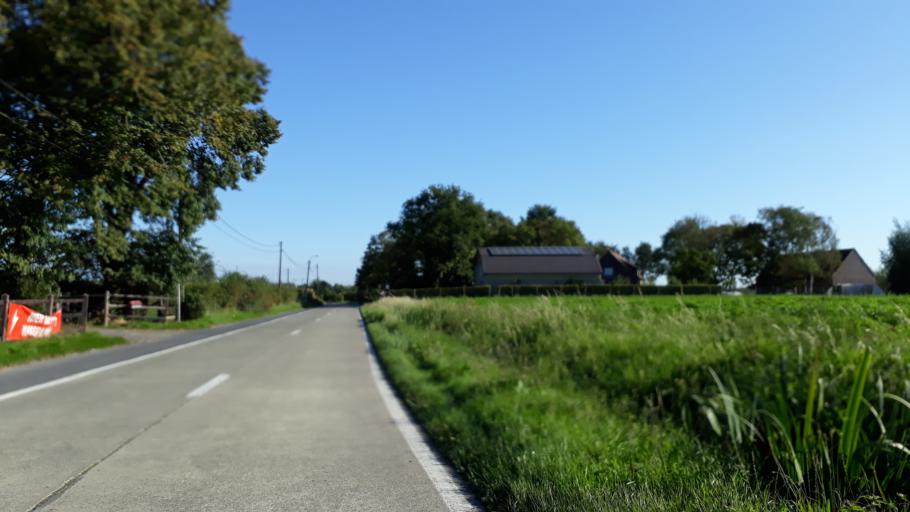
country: BE
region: Flanders
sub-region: Provincie West-Vlaanderen
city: Torhout
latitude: 51.0894
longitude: 3.1409
